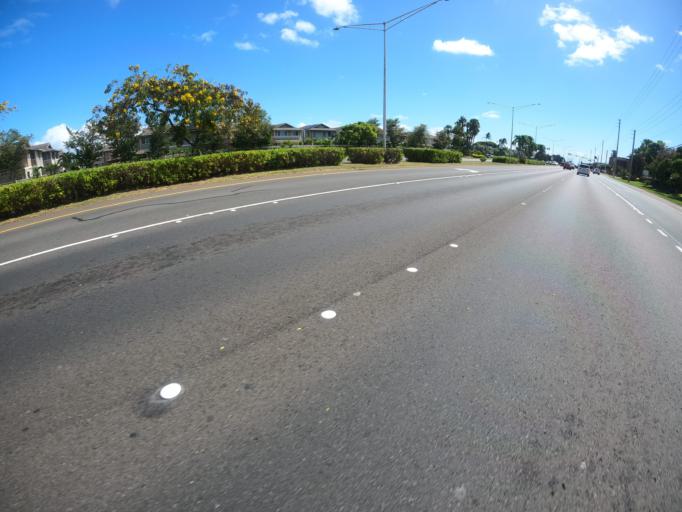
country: US
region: Hawaii
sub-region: Honolulu County
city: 'Ewa Gentry
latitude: 21.3300
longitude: -158.0213
